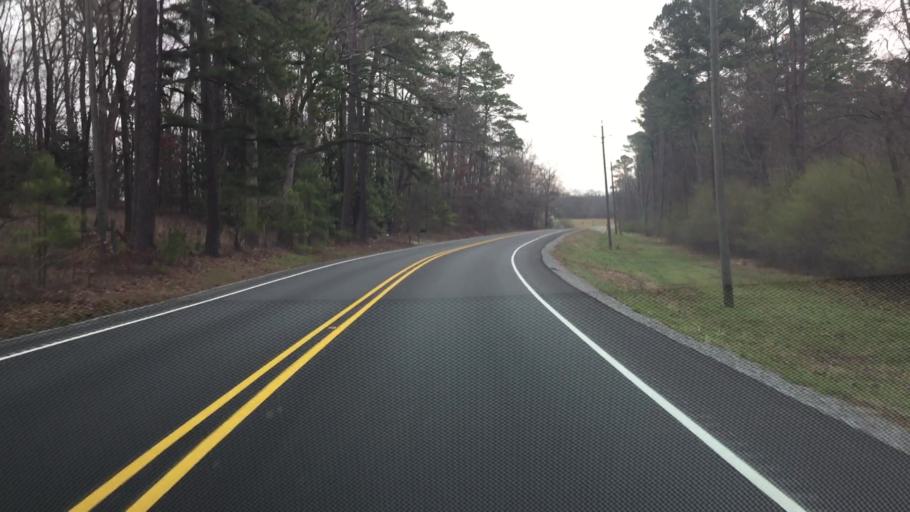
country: US
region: Arkansas
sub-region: Saline County
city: Haskell
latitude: 34.6161
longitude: -92.7856
